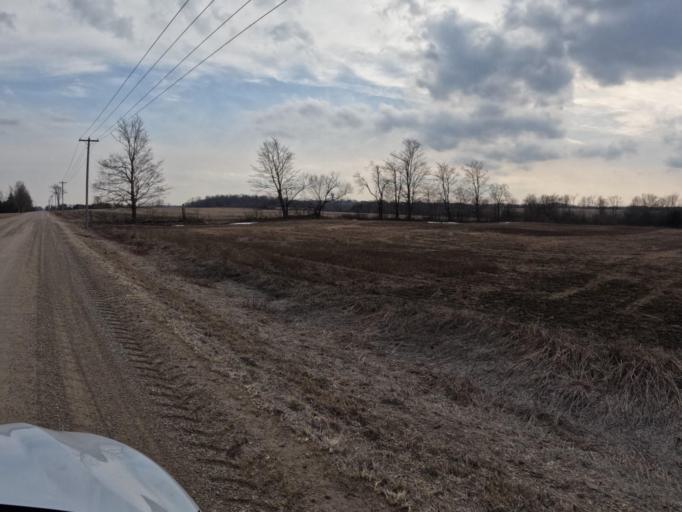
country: CA
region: Ontario
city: Shelburne
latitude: 43.9215
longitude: -80.3062
